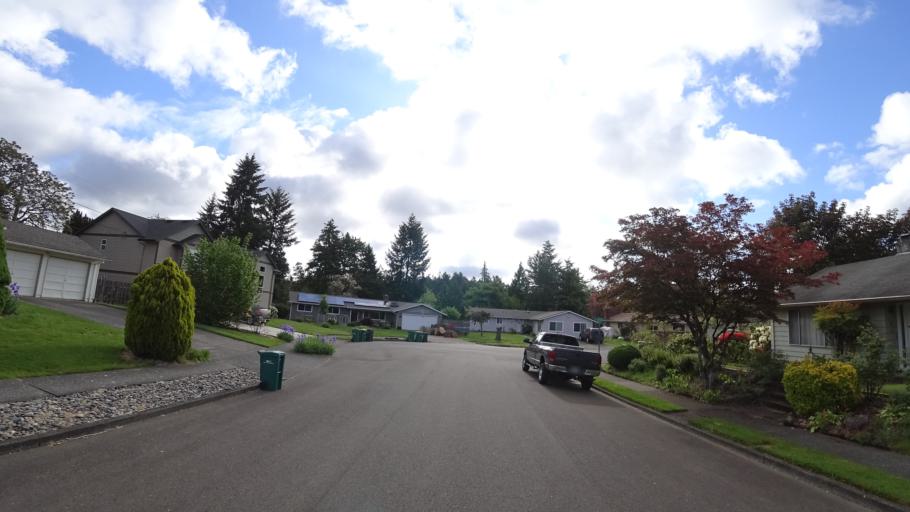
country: US
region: Oregon
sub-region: Washington County
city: Beaverton
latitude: 45.4726
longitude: -122.8168
